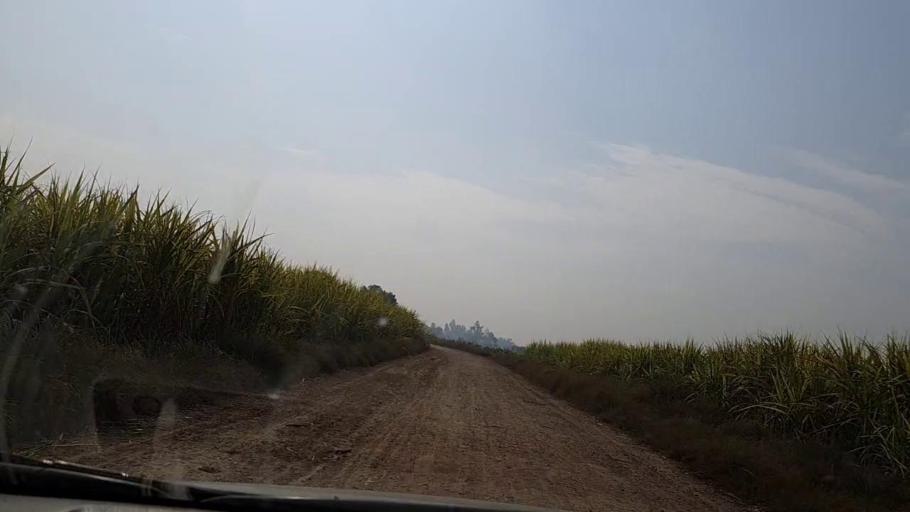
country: PK
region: Sindh
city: Daulatpur
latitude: 26.5373
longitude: 67.9868
